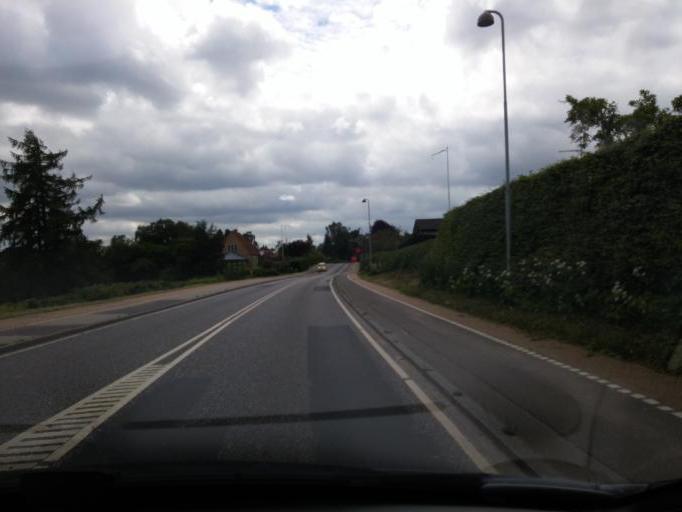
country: DK
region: Capital Region
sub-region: Hillerod Kommune
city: Nodebo
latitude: 55.9876
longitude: 12.3478
